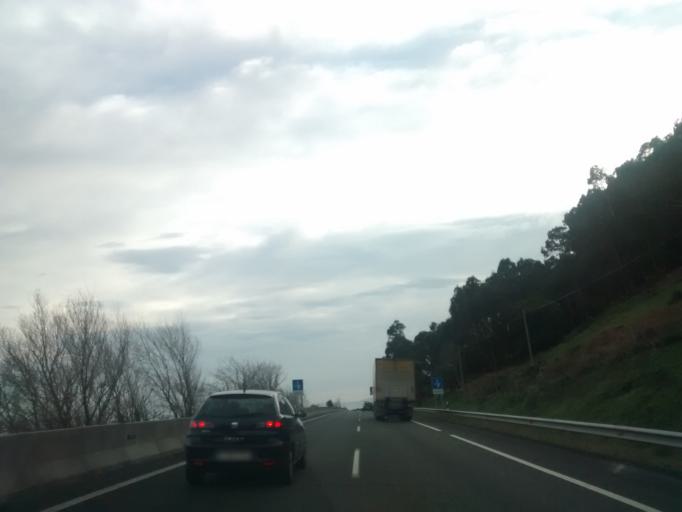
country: ES
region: Cantabria
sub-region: Provincia de Cantabria
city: Liendo
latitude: 43.4022
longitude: -3.3025
